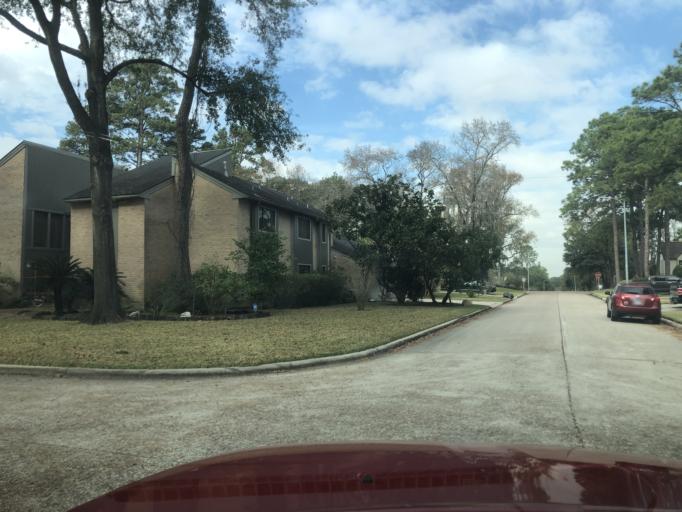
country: US
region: Texas
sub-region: Harris County
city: Spring
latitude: 30.0176
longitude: -95.4657
